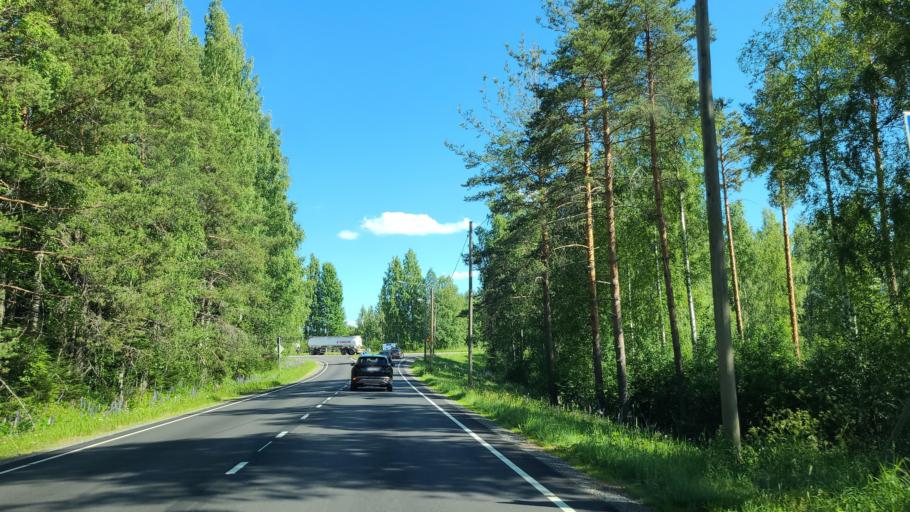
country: FI
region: Central Finland
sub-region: Jyvaeskylae
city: Petaejaevesi
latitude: 62.2582
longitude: 25.1963
